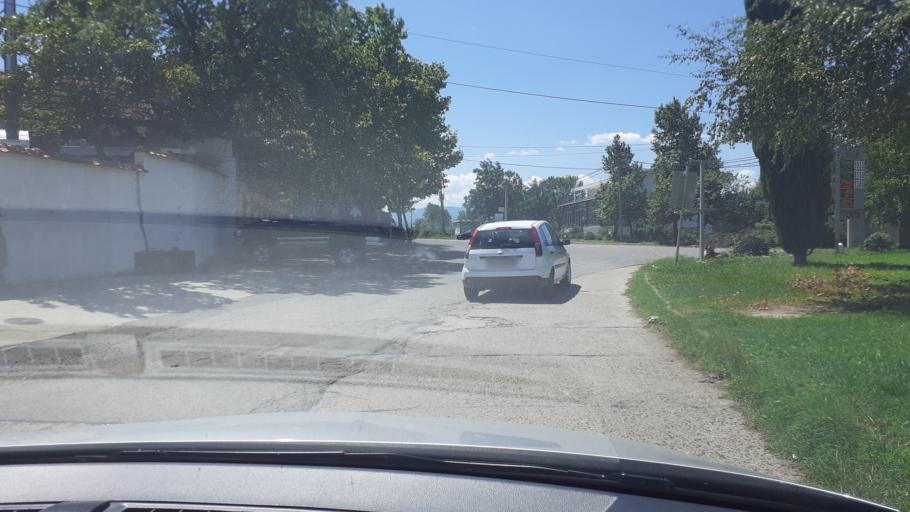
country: MK
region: Gevgelija
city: Gevgelija
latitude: 41.1626
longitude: 22.4963
